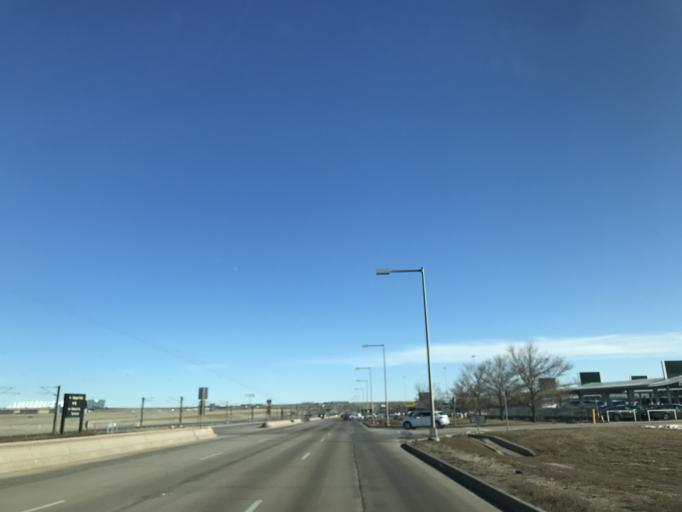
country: US
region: Colorado
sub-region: Adams County
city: Aurora
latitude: 39.8379
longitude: -104.7035
